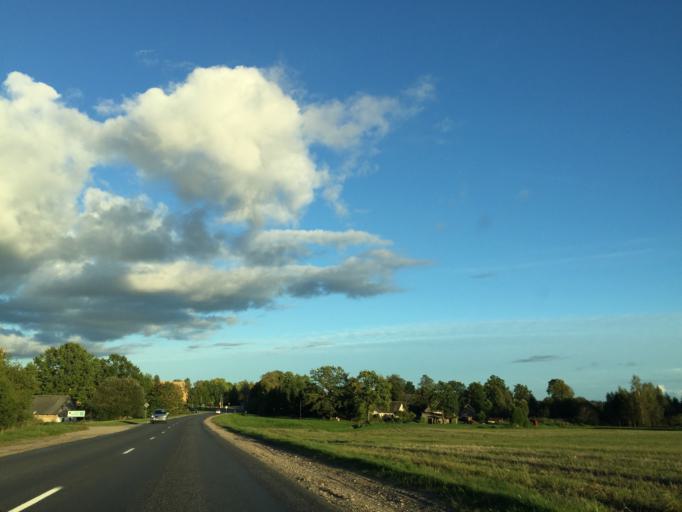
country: LV
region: Saldus Rajons
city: Saldus
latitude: 56.6944
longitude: 22.4416
